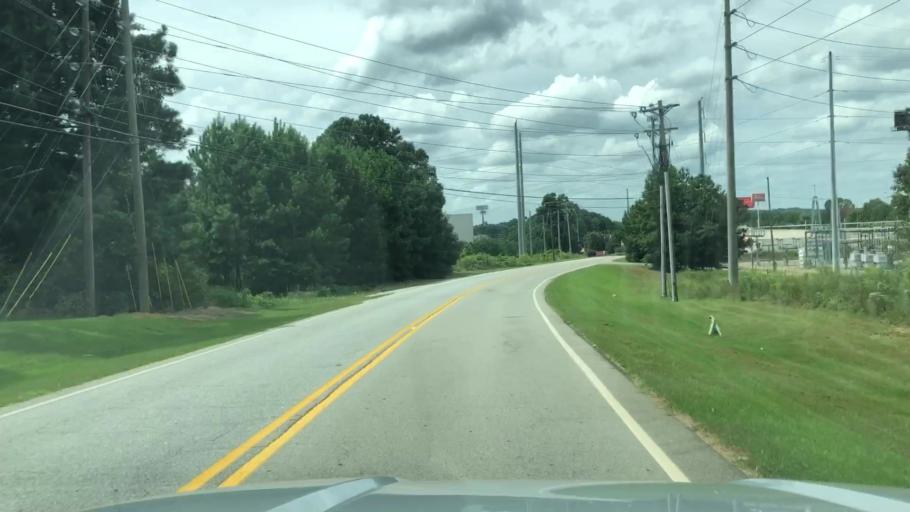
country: US
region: Georgia
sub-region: Gwinnett County
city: Suwanee
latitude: 34.0345
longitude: -84.0391
